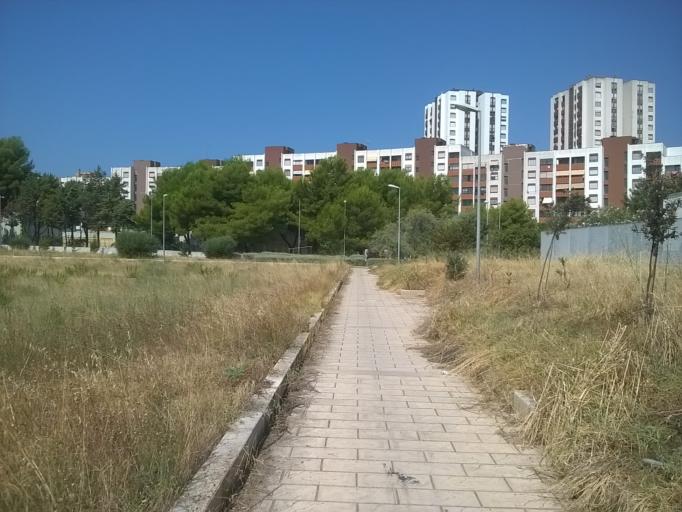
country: IT
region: Apulia
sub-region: Provincia di Taranto
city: Taranto
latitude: 40.4631
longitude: 17.2756
